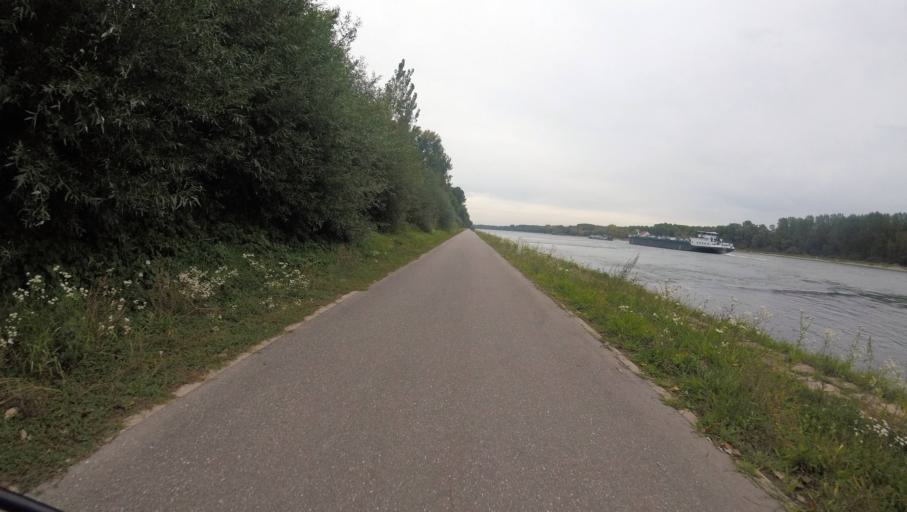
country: DE
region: Rheinland-Pfalz
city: Neuburg
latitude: 48.9752
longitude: 8.2478
